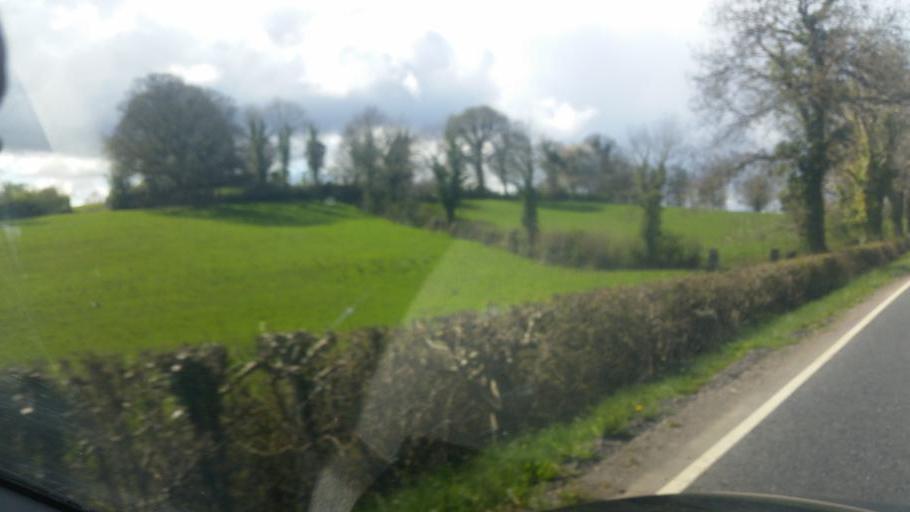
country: GB
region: Northern Ireland
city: Irvinestown
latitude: 54.4269
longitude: -7.7651
